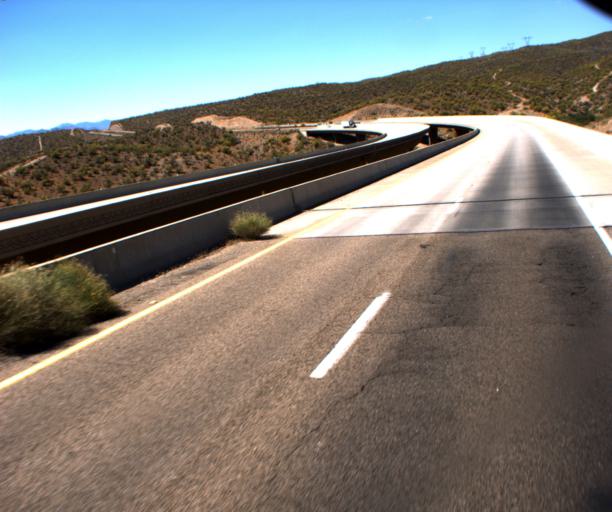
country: US
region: Arizona
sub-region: Yavapai County
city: Bagdad
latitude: 34.5764
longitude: -113.4899
